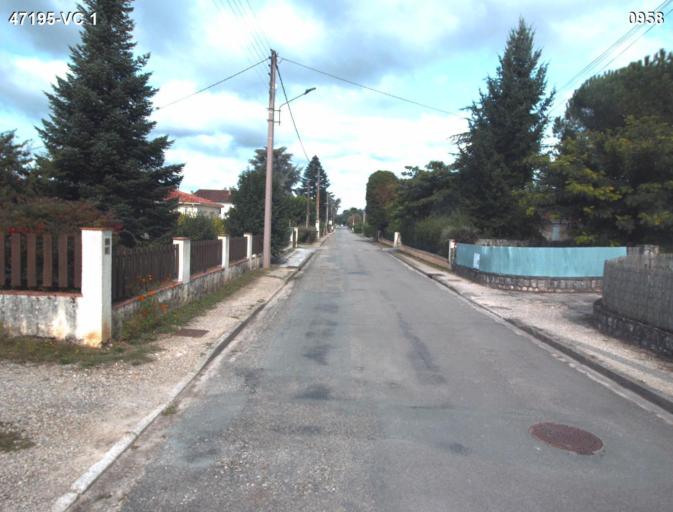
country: FR
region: Aquitaine
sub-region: Departement du Lot-et-Garonne
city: Nerac
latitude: 44.1245
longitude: 0.3455
